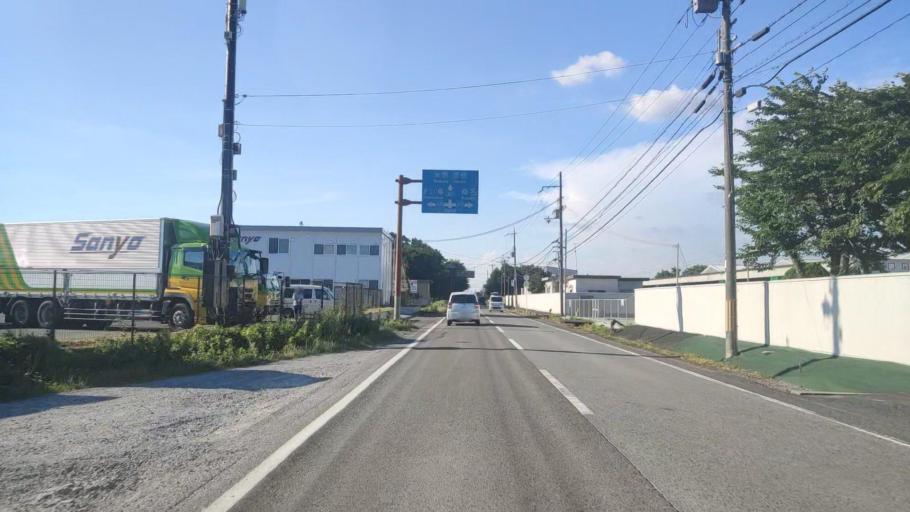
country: JP
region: Shiga Prefecture
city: Youkaichi
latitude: 35.0854
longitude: 136.2503
